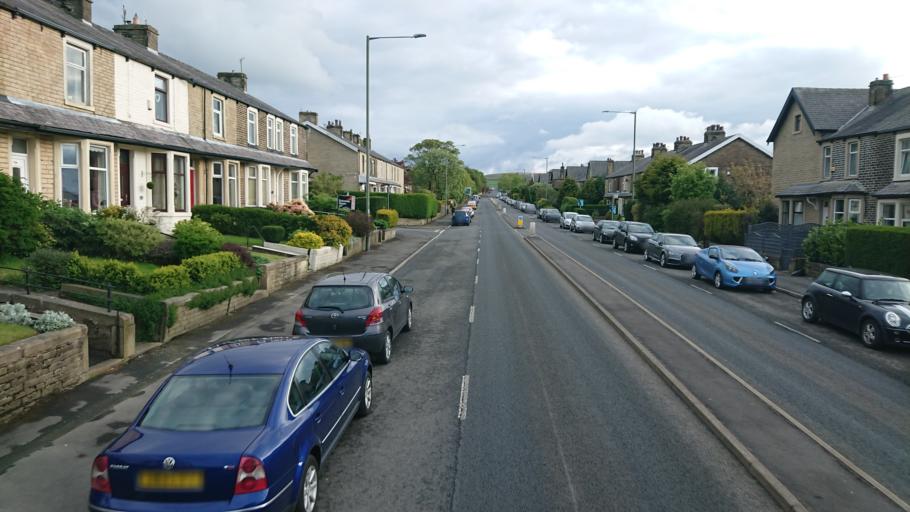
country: GB
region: England
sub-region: Lancashire
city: Burnley
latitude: 53.7766
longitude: -2.2548
